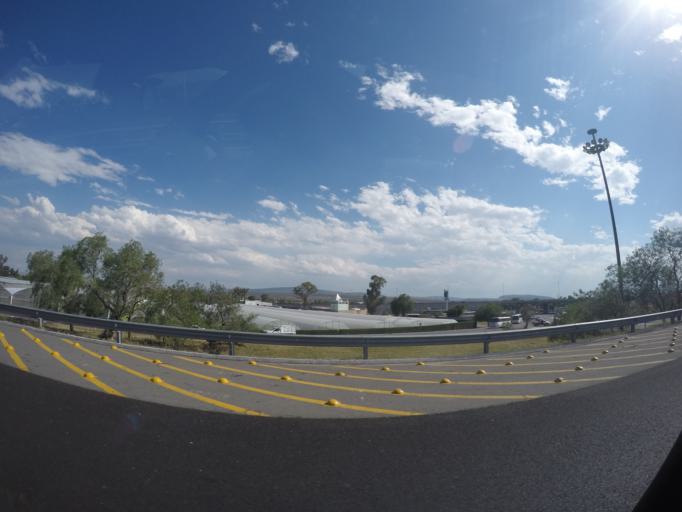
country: MX
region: Guanajuato
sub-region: Apaseo el Grande
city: La Labor
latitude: 20.5362
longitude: -100.7054
